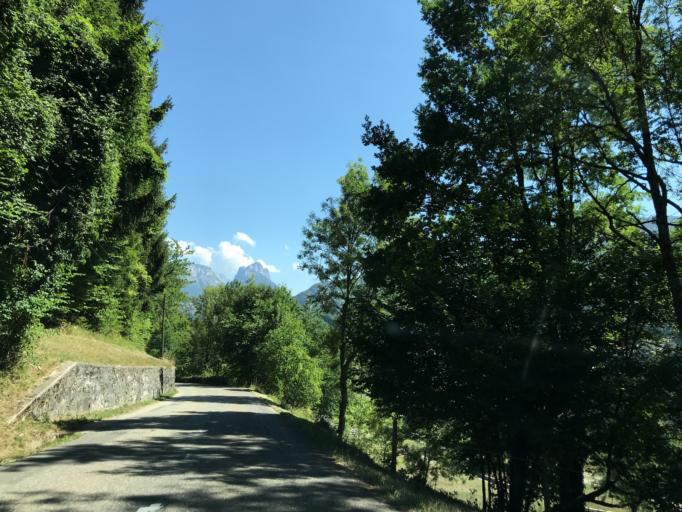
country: FR
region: Rhone-Alpes
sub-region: Departement de la Haute-Savoie
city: Villaz
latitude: 45.9305
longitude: 6.1849
